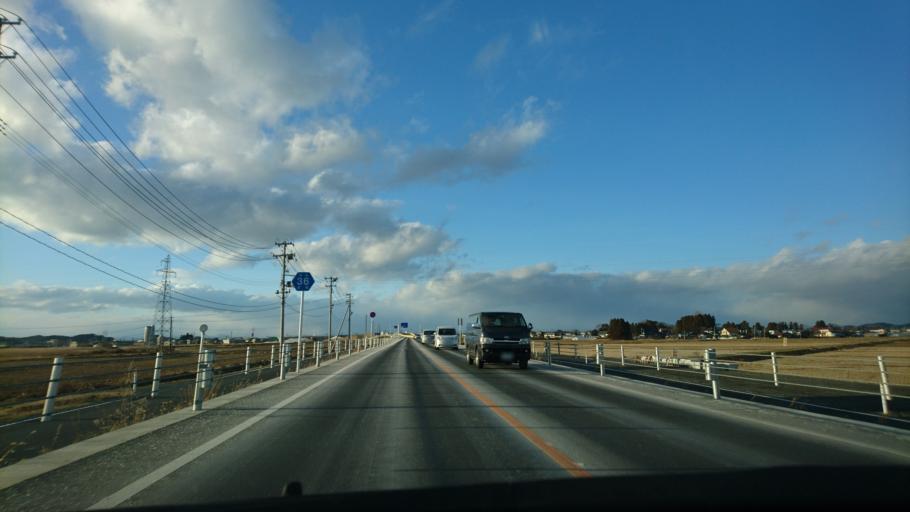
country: JP
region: Miyagi
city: Wakuya
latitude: 38.6909
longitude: 141.2190
